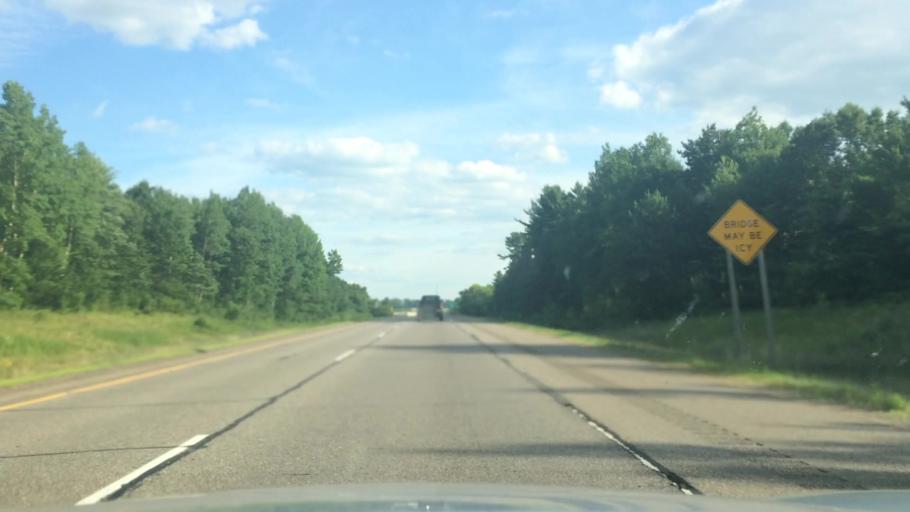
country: US
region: Wisconsin
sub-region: Lincoln County
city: Merrill
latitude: 45.1420
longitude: -89.6415
